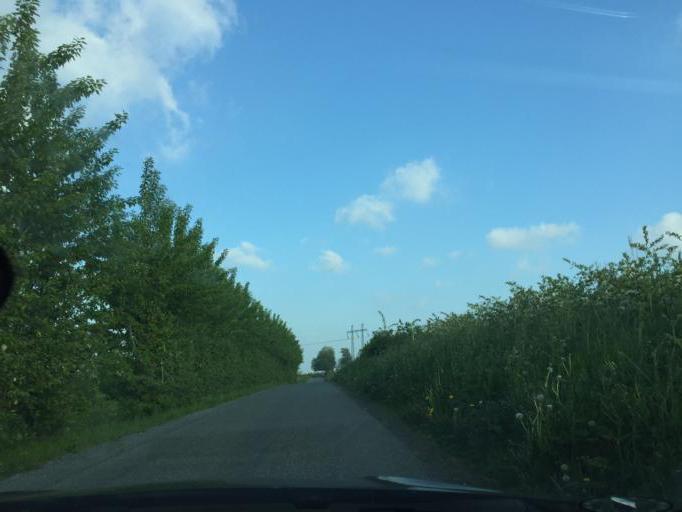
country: DK
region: South Denmark
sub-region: Odense Kommune
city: Bellinge
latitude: 55.3833
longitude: 10.2923
